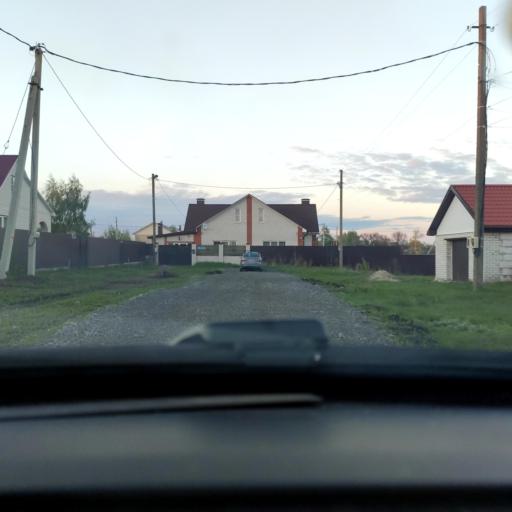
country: RU
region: Voronezj
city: Novaya Usman'
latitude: 51.6562
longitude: 39.4243
